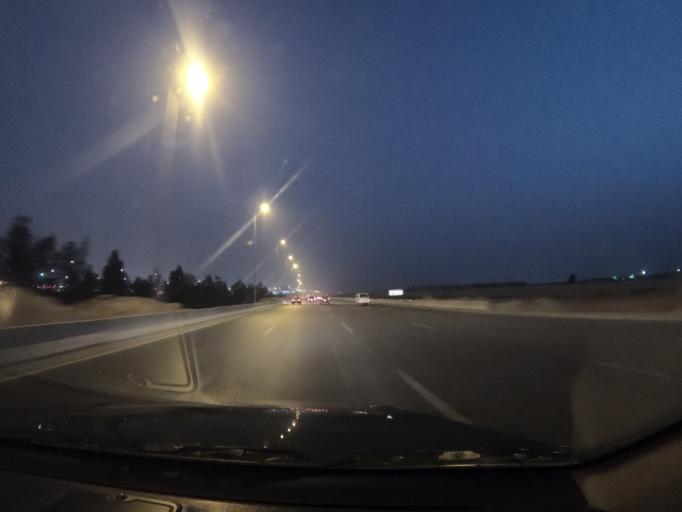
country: EG
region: Muhafazat al Qahirah
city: Cairo
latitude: 30.0356
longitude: 31.4025
